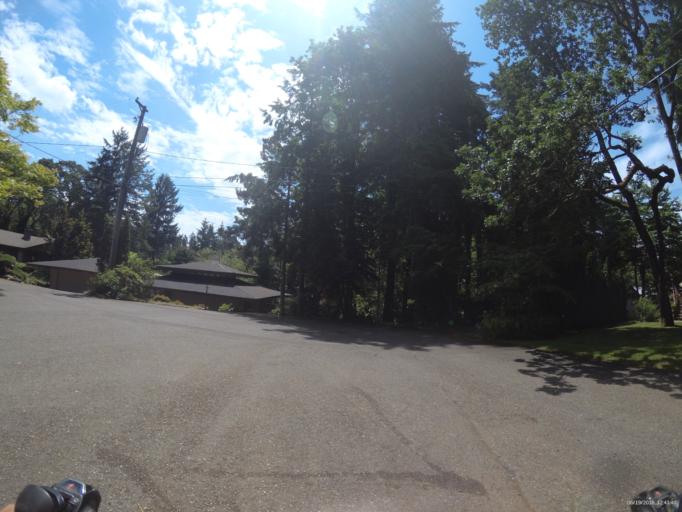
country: US
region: Washington
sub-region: Pierce County
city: Lakewood
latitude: 47.1626
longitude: -122.5251
